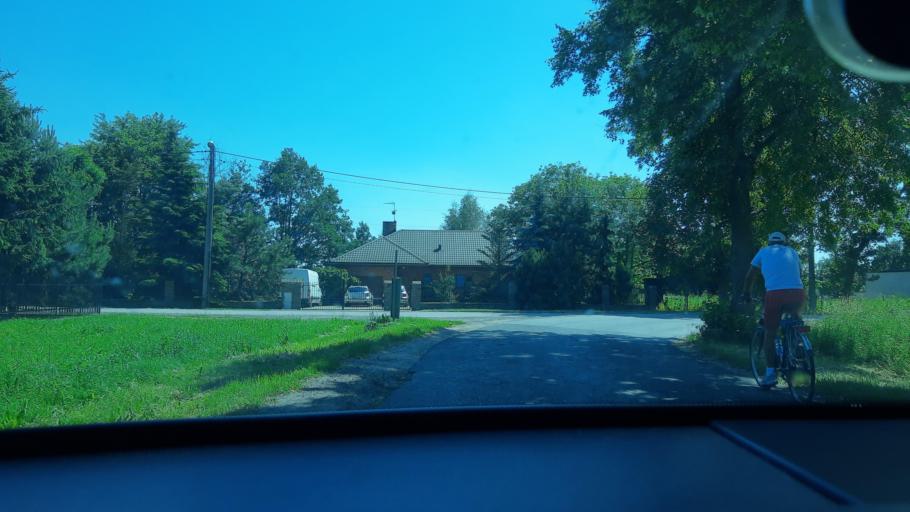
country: PL
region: Lodz Voivodeship
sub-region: Powiat zdunskowolski
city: Zdunska Wola
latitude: 51.6175
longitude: 18.9711
